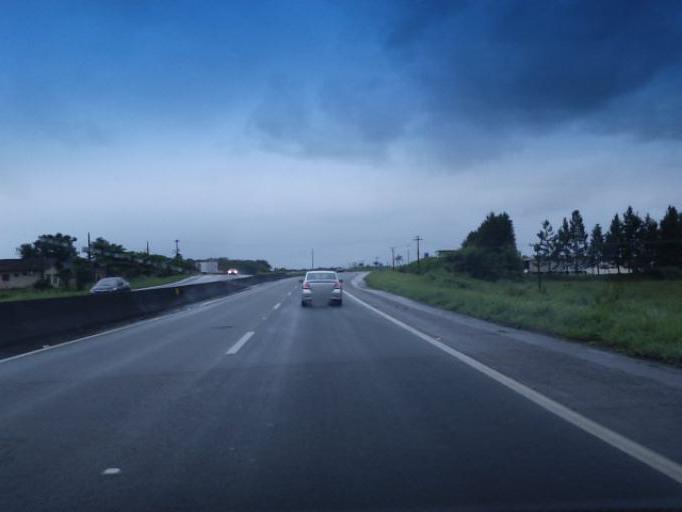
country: BR
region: Santa Catarina
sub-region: Barra Velha
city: Barra Velha
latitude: -26.4884
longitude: -48.7342
